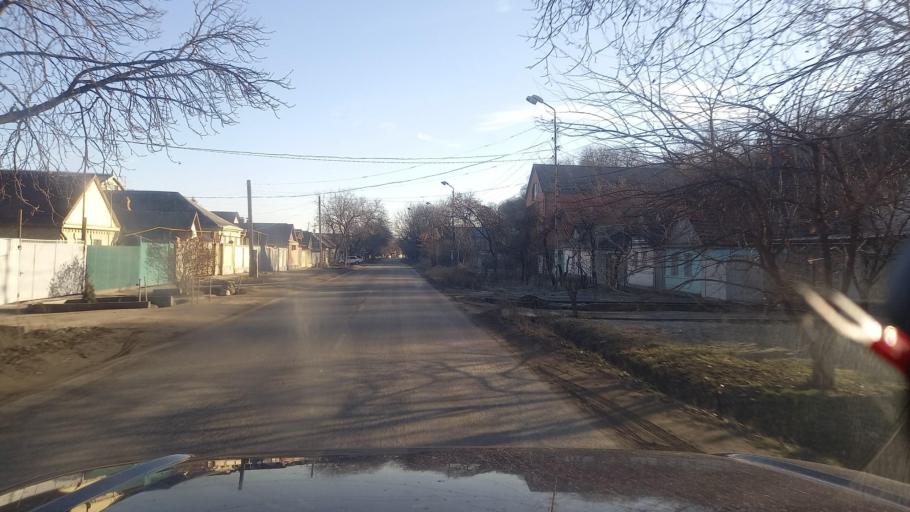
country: RU
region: Stavropol'skiy
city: Svobody
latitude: 44.0237
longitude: 43.0543
